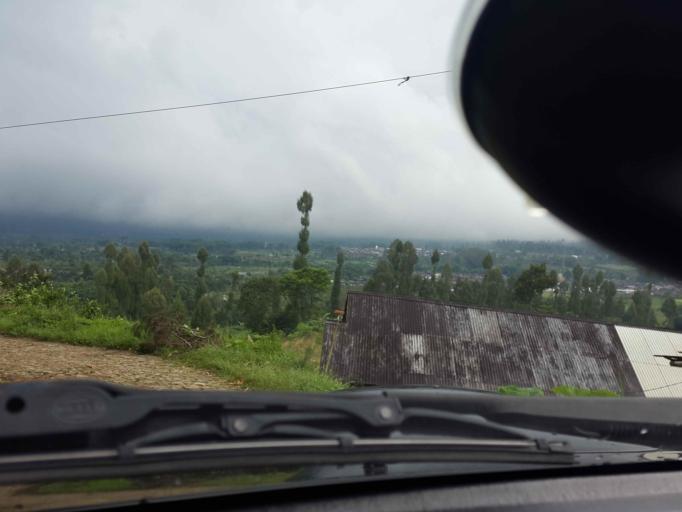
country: ID
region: Central Java
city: Wonosobo
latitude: -7.3633
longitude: 110.0147
